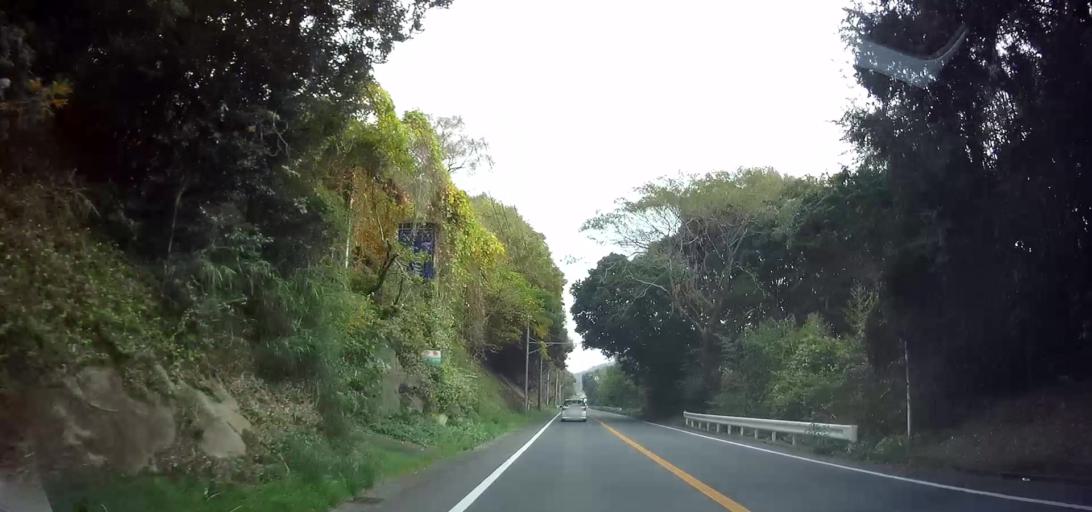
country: JP
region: Nagasaki
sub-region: Isahaya-shi
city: Isahaya
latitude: 32.7994
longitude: 130.1267
